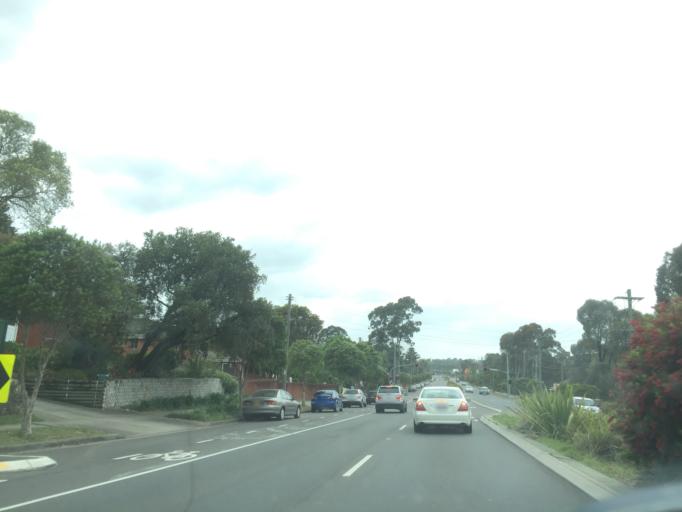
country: AU
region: New South Wales
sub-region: Blacktown
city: Blacktown
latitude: -33.7676
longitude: 150.9474
